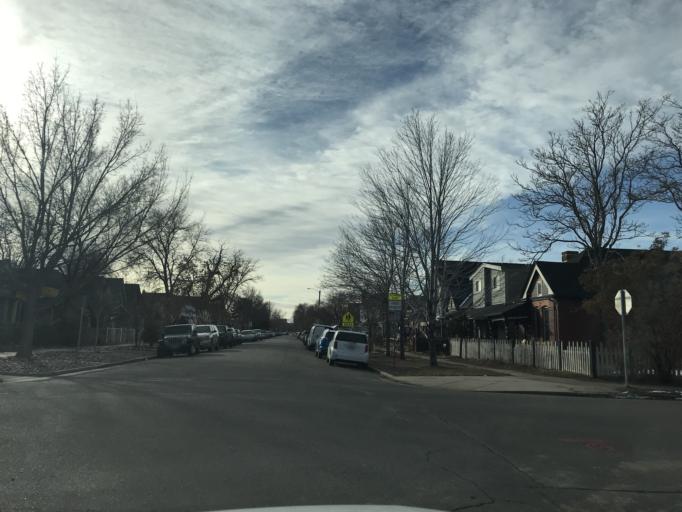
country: US
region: Colorado
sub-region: Denver County
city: Denver
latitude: 39.7702
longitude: -104.9672
